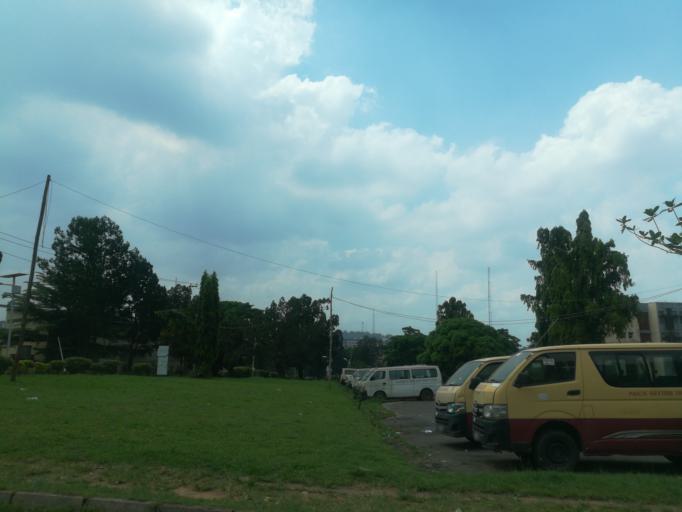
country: NG
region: Oyo
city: Ibadan
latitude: 7.4096
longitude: 3.9049
